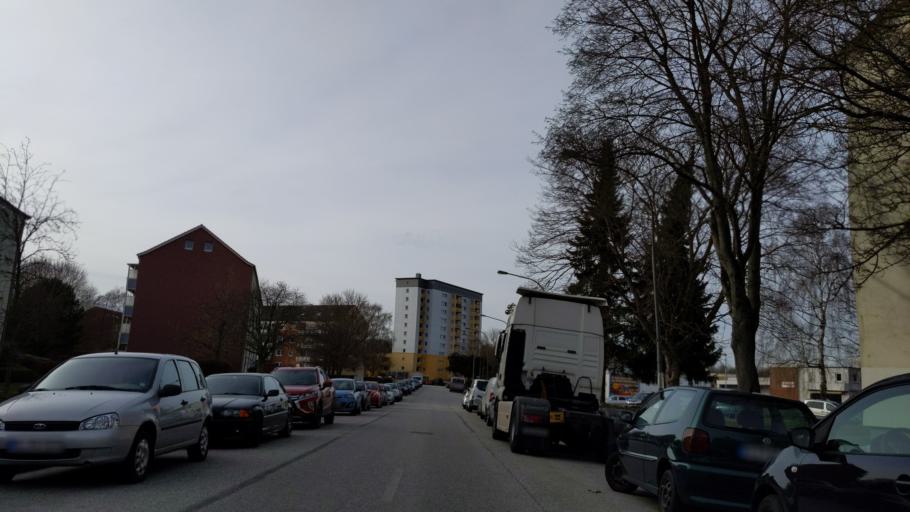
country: DE
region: Mecklenburg-Vorpommern
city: Selmsdorf
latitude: 53.9222
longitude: 10.8223
